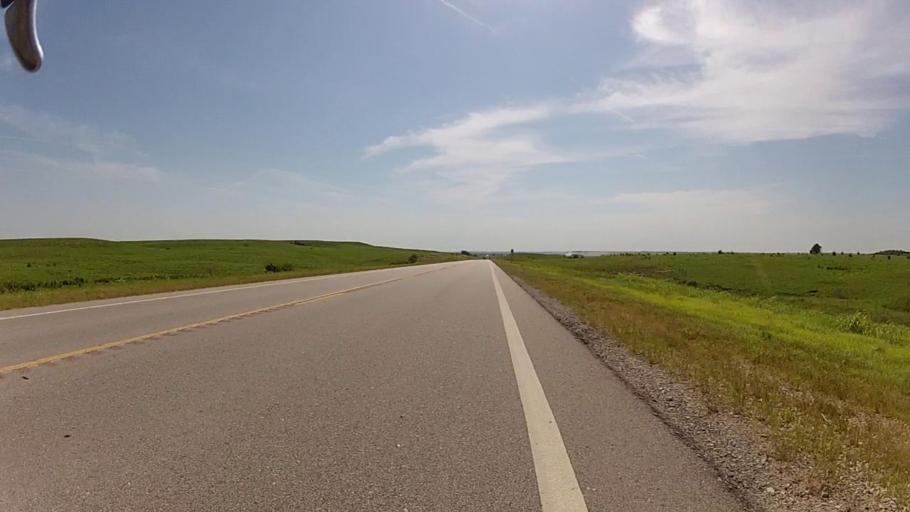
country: US
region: Kansas
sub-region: Cowley County
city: Winfield
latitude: 37.1106
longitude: -96.6417
